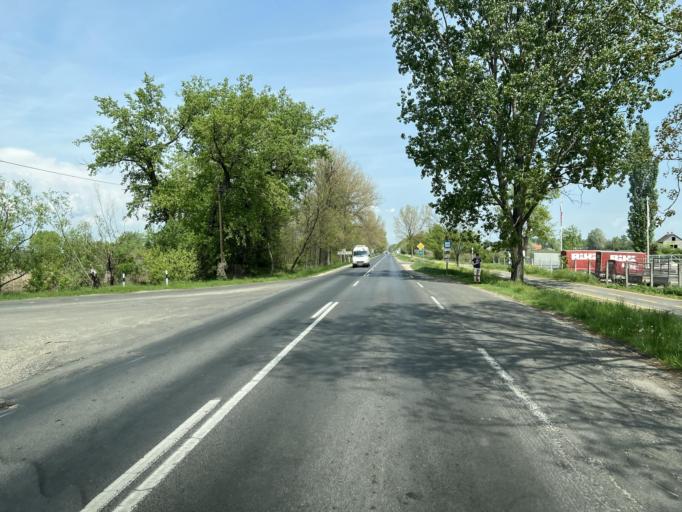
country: HU
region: Pest
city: Cegled
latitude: 47.1395
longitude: 19.7885
